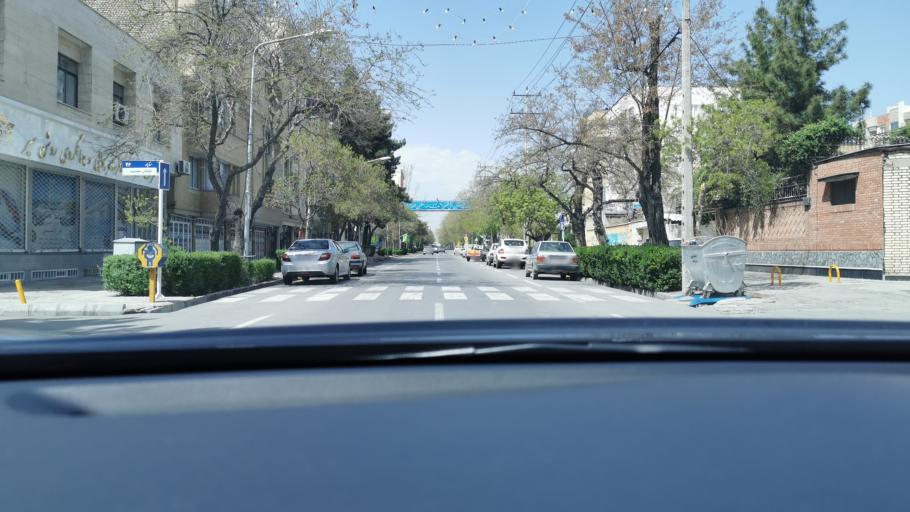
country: IR
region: Razavi Khorasan
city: Mashhad
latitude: 36.2990
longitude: 59.5899
